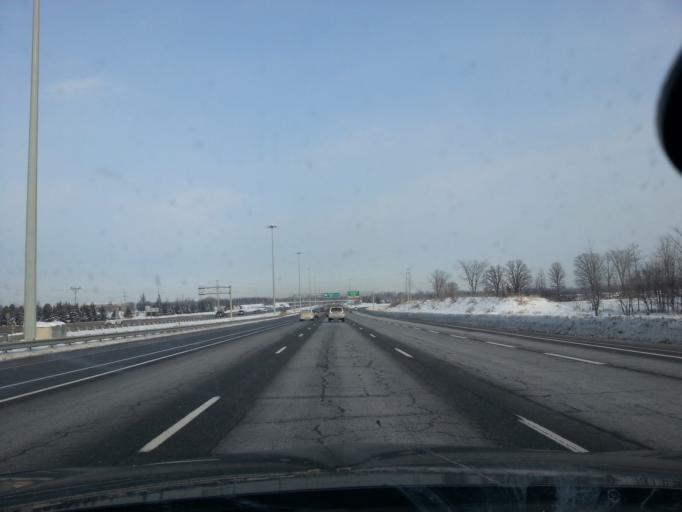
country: CA
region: Ontario
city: Bells Corners
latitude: 45.3350
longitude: -75.8493
